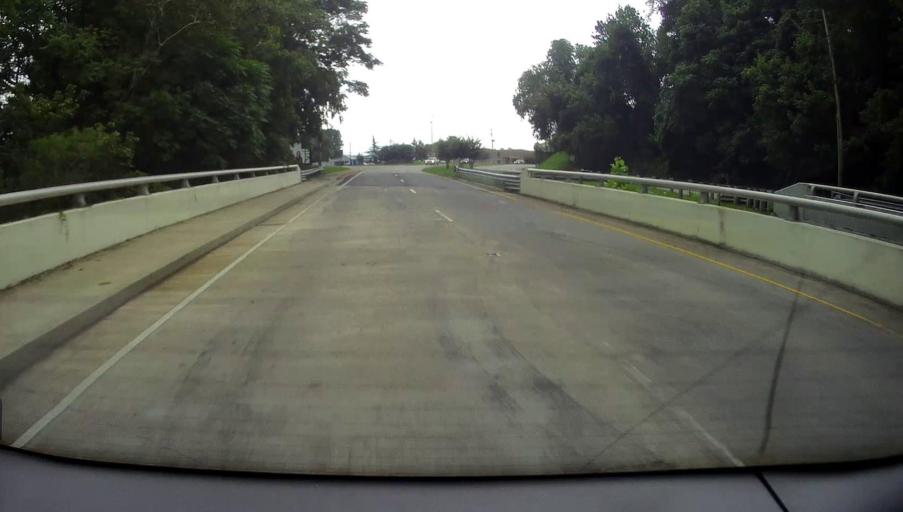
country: US
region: Tennessee
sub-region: Coffee County
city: Manchester
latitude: 35.4861
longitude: -86.0905
